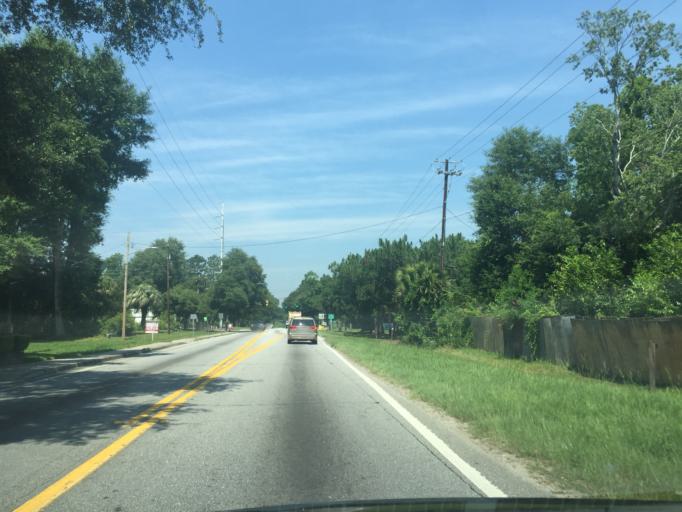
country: US
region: Georgia
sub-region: Chatham County
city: Savannah
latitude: 32.0525
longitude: -81.1350
